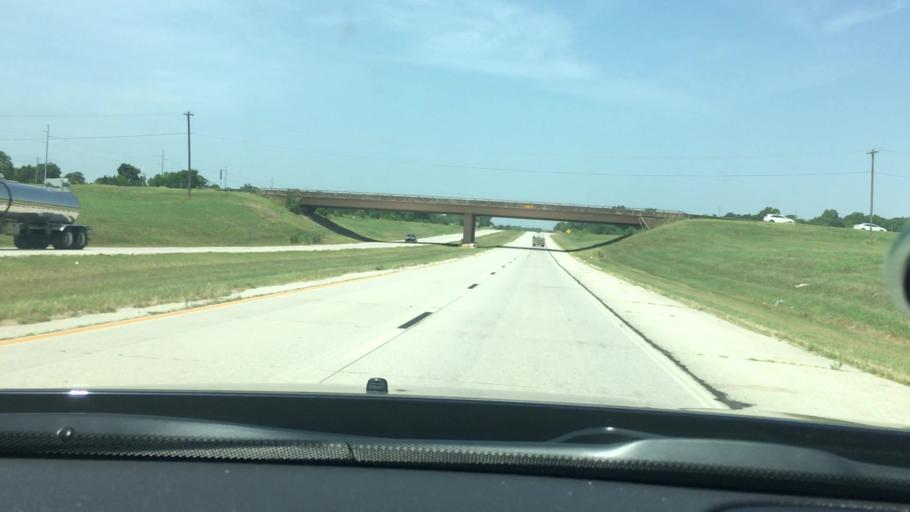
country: US
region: Oklahoma
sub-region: Pontotoc County
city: Ada
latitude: 34.7524
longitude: -96.6683
